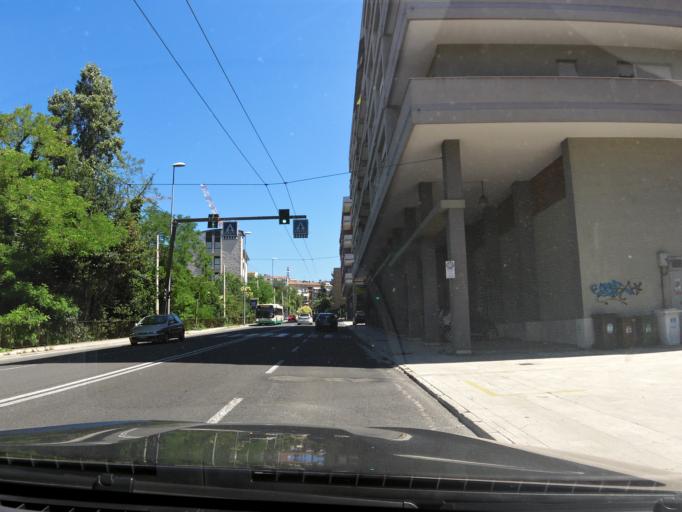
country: IT
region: The Marches
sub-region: Provincia di Ancona
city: Le Grazie di Ancona
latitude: 43.6072
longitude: 13.5148
